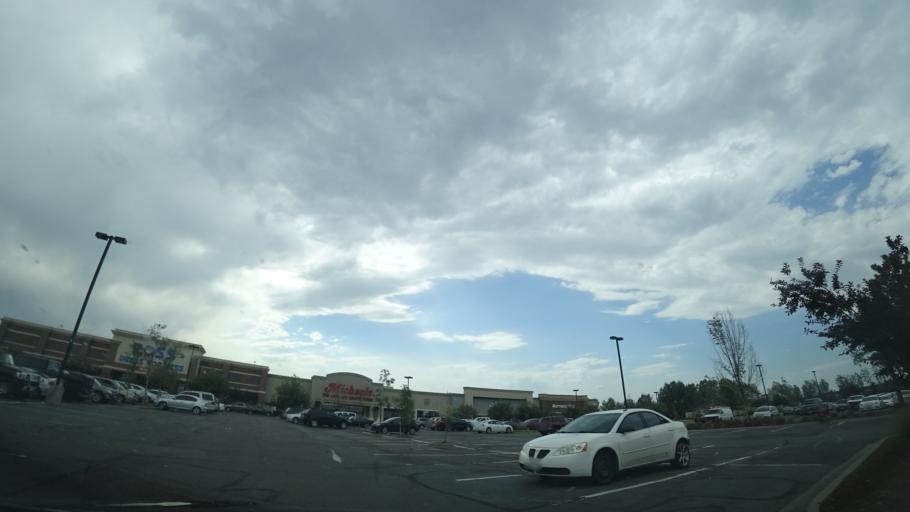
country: US
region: Colorado
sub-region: Jefferson County
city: Lakewood
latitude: 39.7081
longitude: -105.0822
